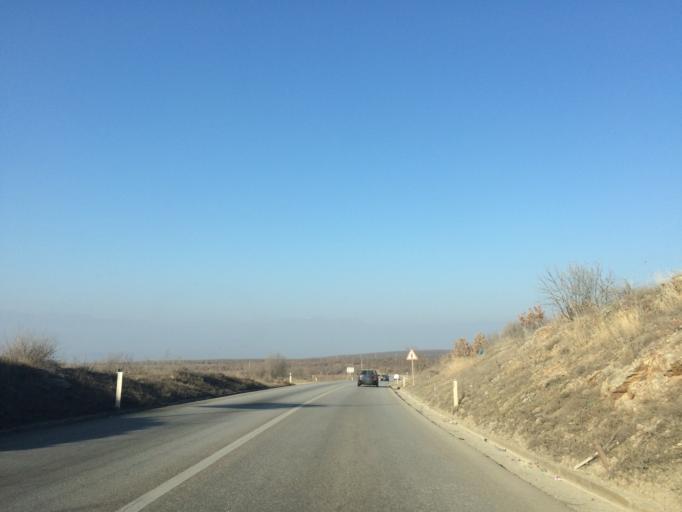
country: XK
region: Pec
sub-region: Komuna e Klines
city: Klina
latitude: 42.5953
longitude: 20.6294
